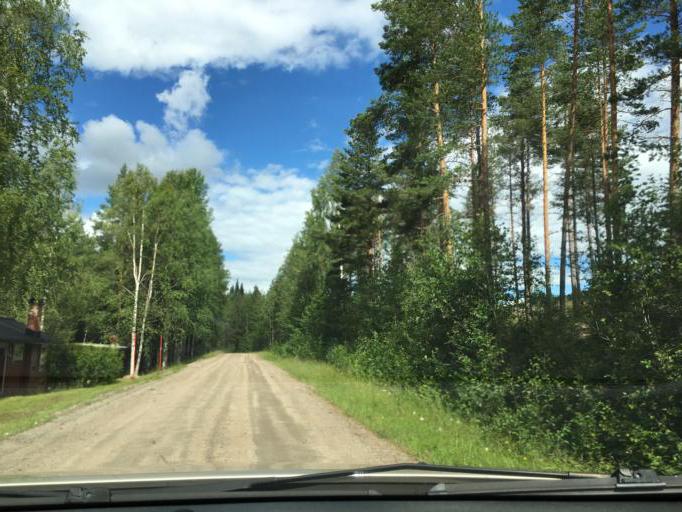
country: SE
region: Norrbotten
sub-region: Overkalix Kommun
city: OEverkalix
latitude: 66.1303
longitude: 22.7847
